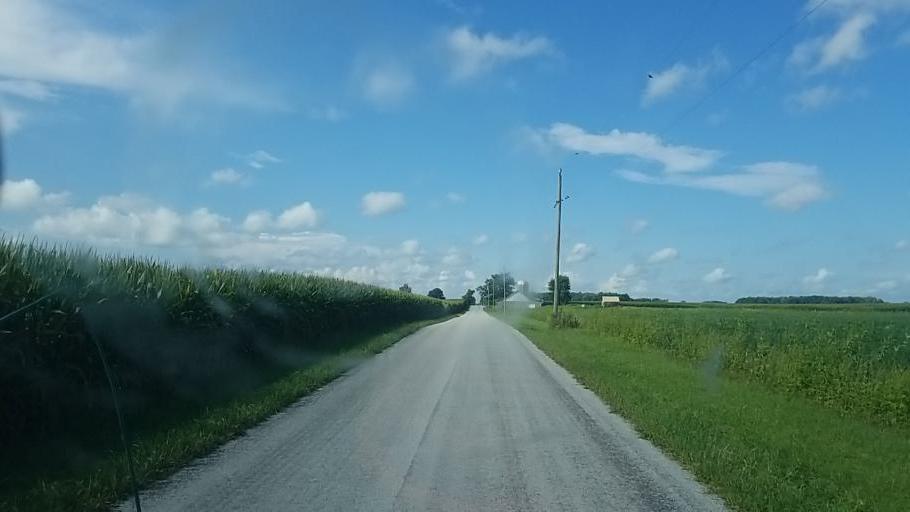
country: US
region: Ohio
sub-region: Hardin County
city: Kenton
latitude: 40.6786
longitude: -83.5310
